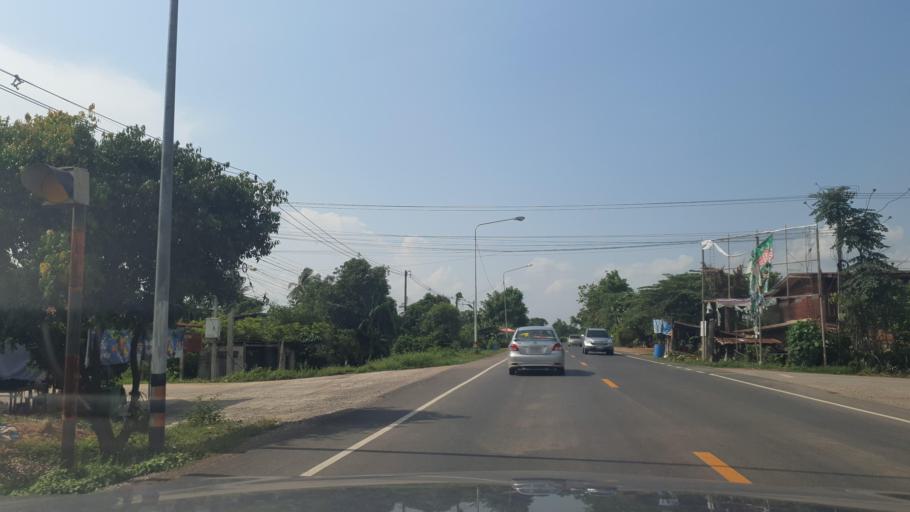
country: TH
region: Sukhothai
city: Si Samrong
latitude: 17.2037
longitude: 99.8490
